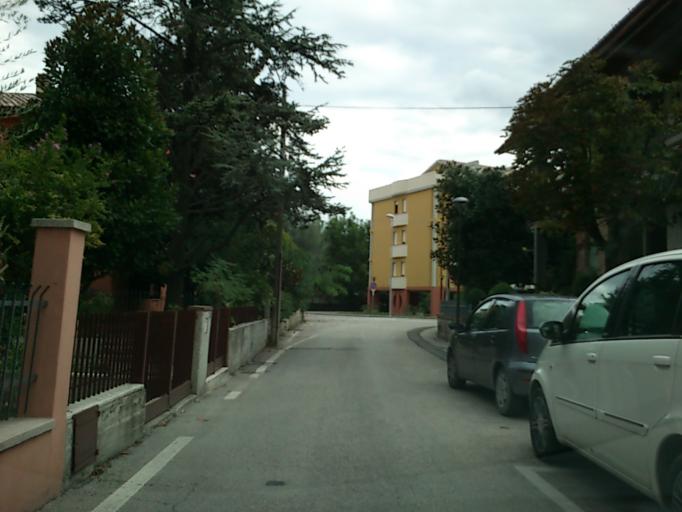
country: IT
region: The Marches
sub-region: Provincia di Pesaro e Urbino
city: Lucrezia
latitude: 43.7733
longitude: 12.9381
